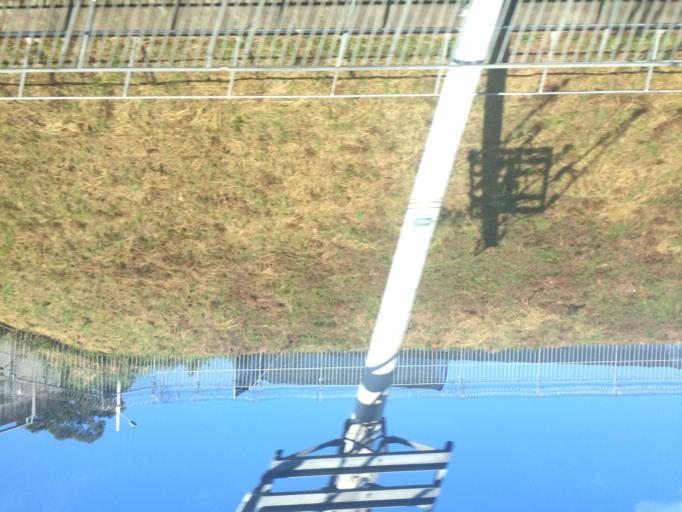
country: TW
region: Taiwan
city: Fengyuan
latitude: 24.3254
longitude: 120.6745
